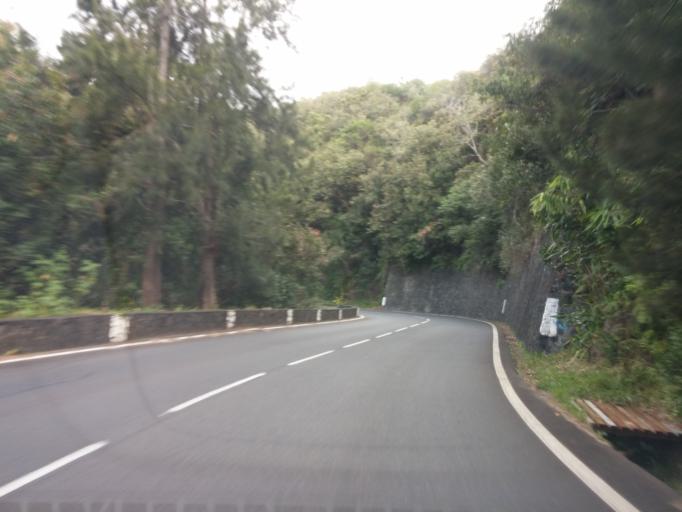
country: RE
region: Reunion
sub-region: Reunion
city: Saint-Denis
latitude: -20.9038
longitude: 55.4180
